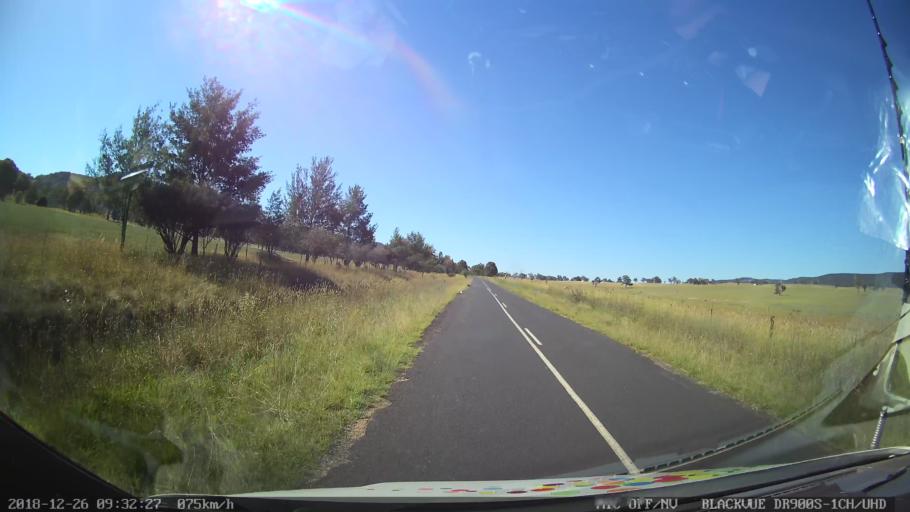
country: AU
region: New South Wales
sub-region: Mid-Western Regional
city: Kandos
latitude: -32.8845
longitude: 150.0324
